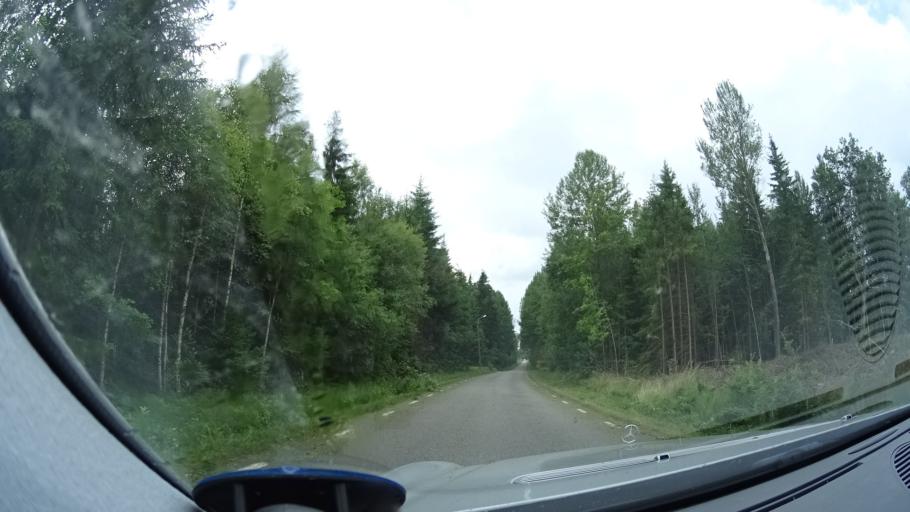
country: SE
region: Kalmar
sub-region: Emmaboda Kommun
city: Emmaboda
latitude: 56.6548
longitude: 15.7104
